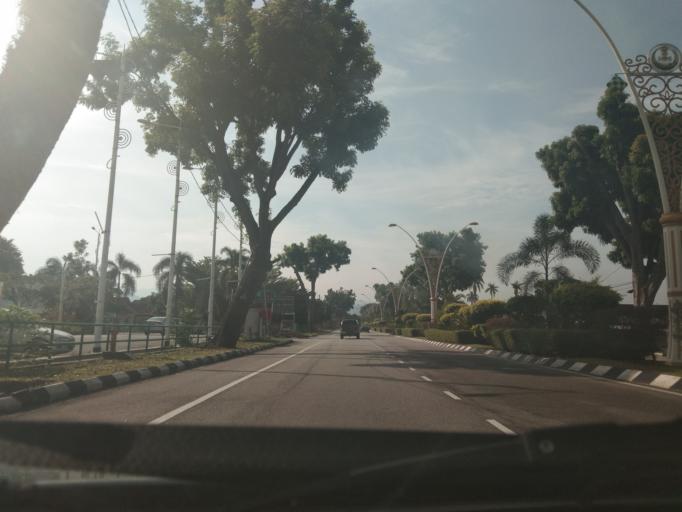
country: MY
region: Perak
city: Ipoh
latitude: 4.5886
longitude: 101.0951
